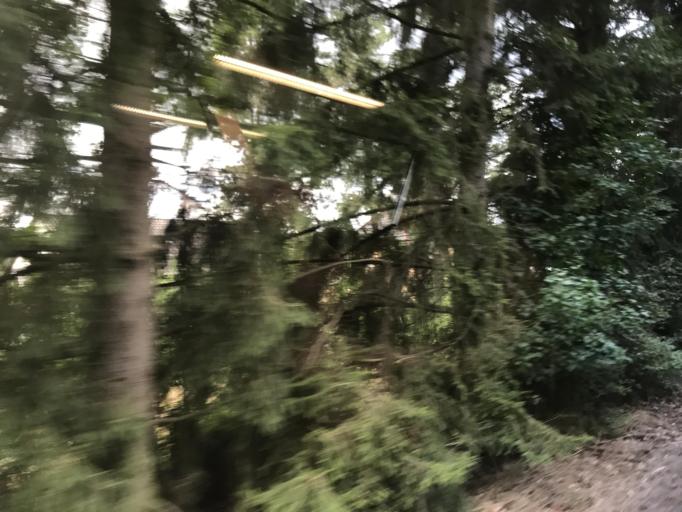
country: DE
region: Bavaria
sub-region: Regierungsbezirk Unterfranken
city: Bad Kissingen
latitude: 50.1840
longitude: 10.0794
